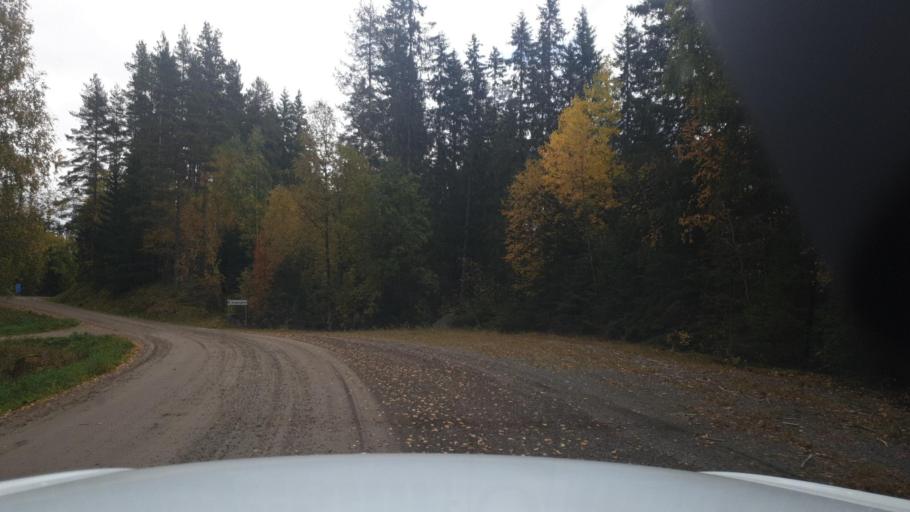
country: SE
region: Vaermland
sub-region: Eda Kommun
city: Charlottenberg
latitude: 60.0707
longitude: 12.5316
